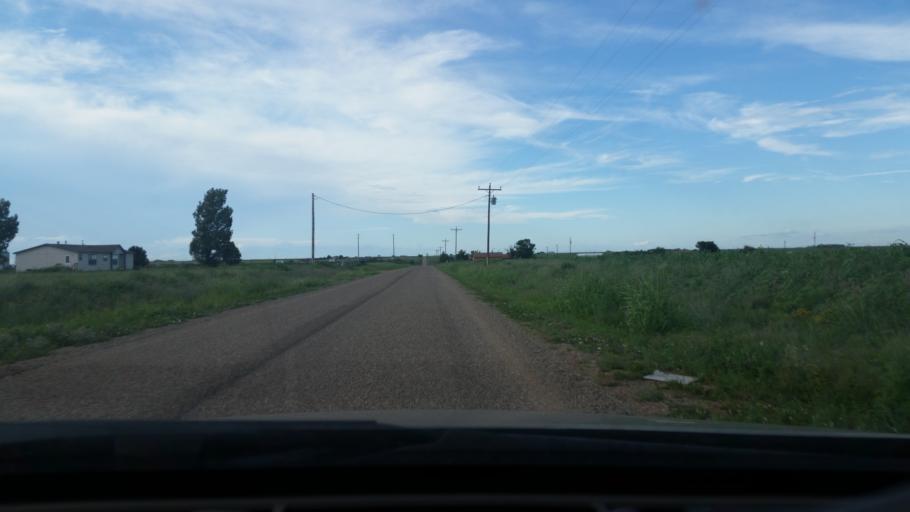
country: US
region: New Mexico
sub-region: Curry County
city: Clovis
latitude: 34.4679
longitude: -103.1789
